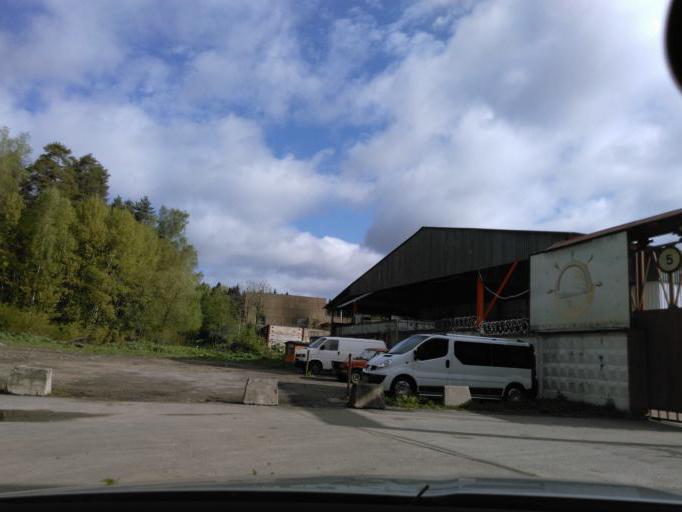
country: RU
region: Moscow
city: Zelenograd
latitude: 56.0058
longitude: 37.1791
